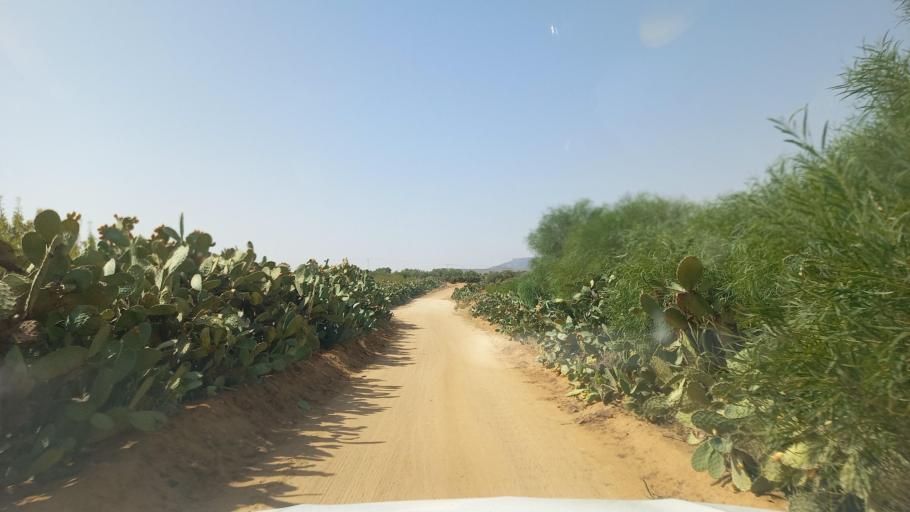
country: TN
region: Al Qasrayn
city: Kasserine
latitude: 35.2394
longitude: 9.0465
